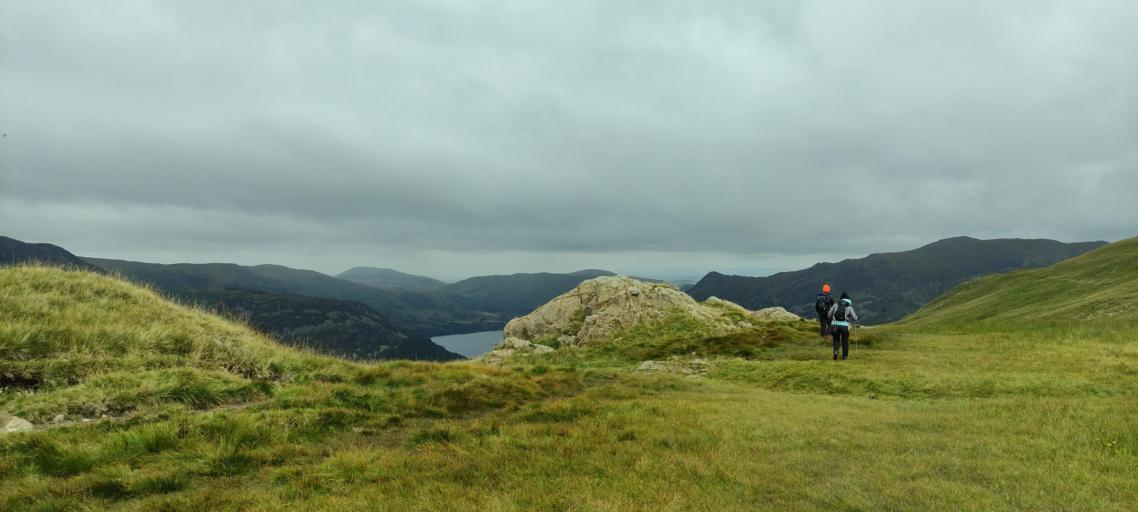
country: GB
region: England
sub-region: Cumbria
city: Ambleside
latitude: 54.5227
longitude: -2.9624
